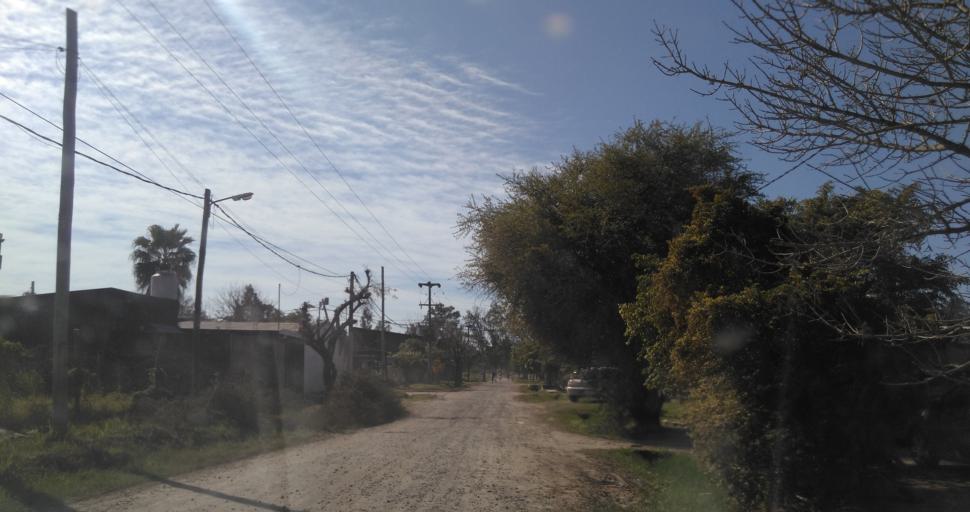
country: AR
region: Chaco
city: Fontana
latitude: -27.4451
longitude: -59.0291
